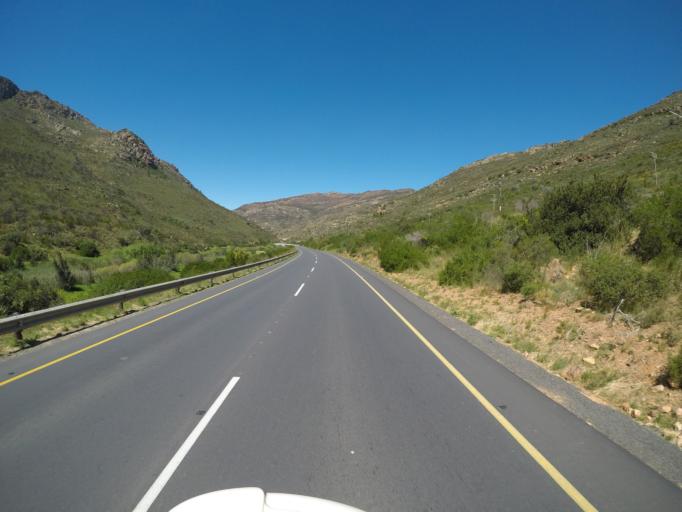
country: ZA
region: Western Cape
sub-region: Cape Winelands District Municipality
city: Ceres
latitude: -33.3087
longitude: 19.0706
